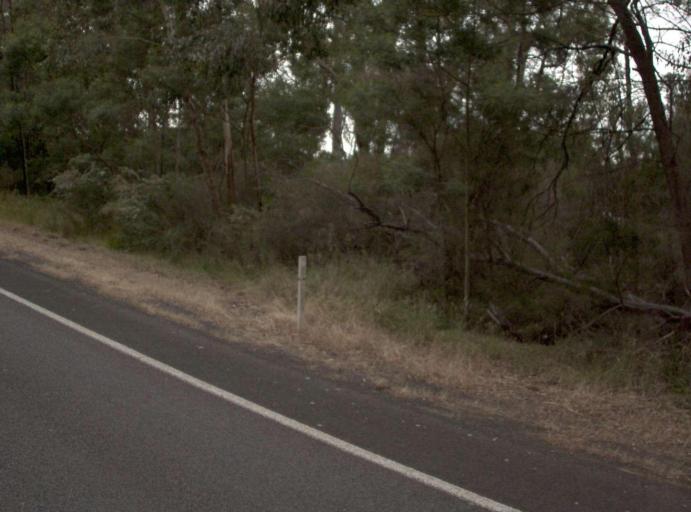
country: AU
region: Victoria
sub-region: Wellington
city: Sale
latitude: -38.4464
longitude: 146.9431
